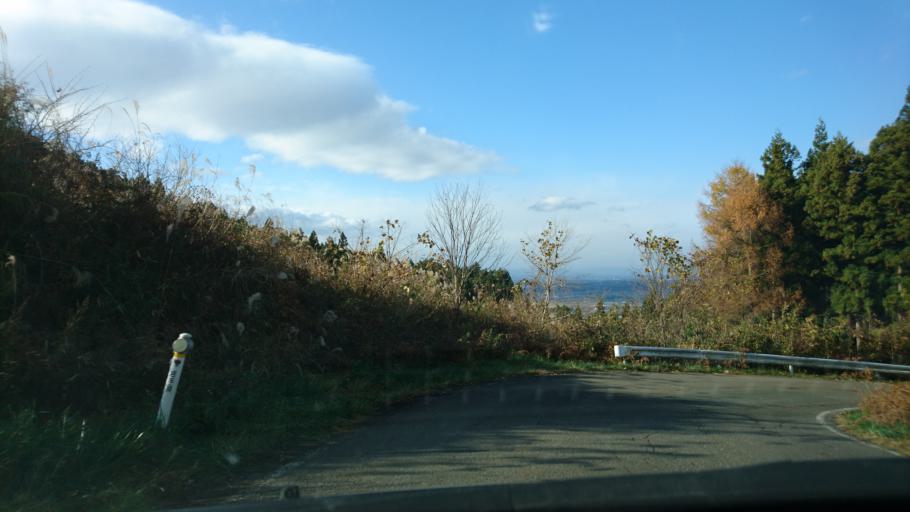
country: JP
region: Iwate
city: Ichinoseki
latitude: 39.0248
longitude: 141.1691
